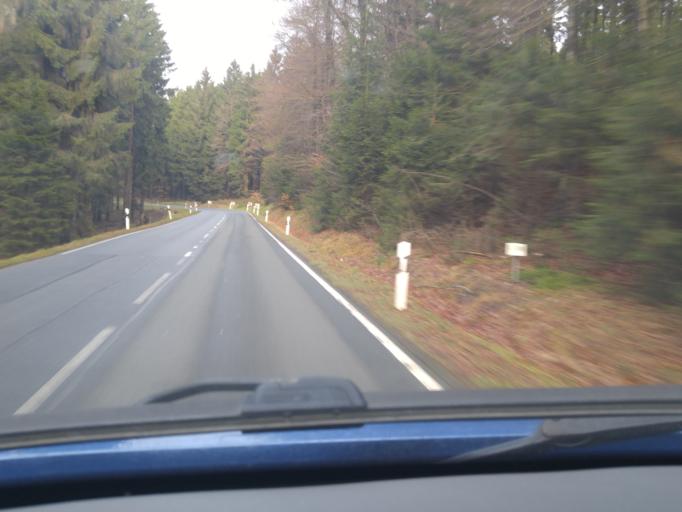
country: DE
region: Hesse
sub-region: Regierungsbezirk Darmstadt
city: Glashutten
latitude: 50.2180
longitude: 8.4359
